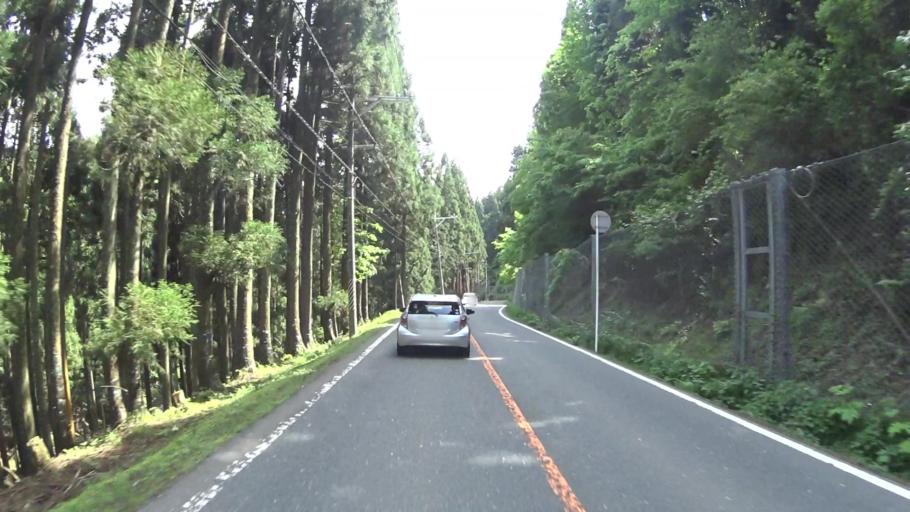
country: JP
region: Shiga Prefecture
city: Kitahama
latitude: 35.3788
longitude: 135.9231
